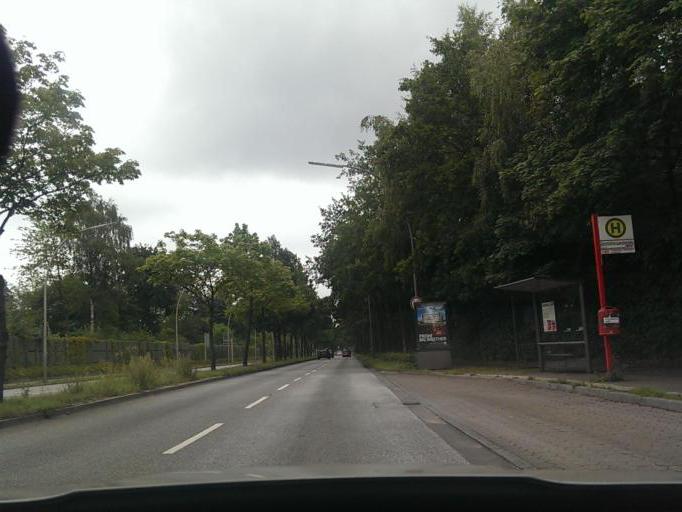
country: DE
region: Hamburg
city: Hummelsbuettel
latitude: 53.6477
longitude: 10.0416
